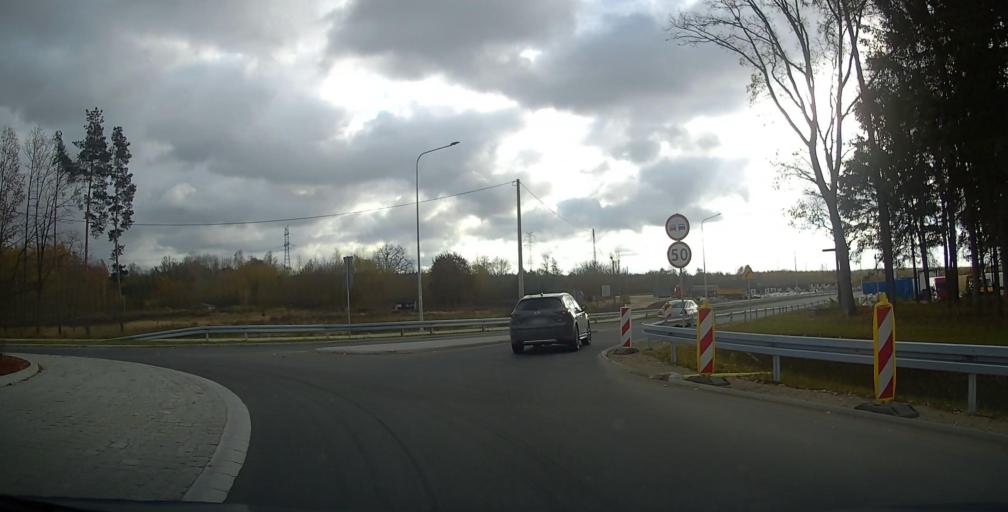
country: PL
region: Warmian-Masurian Voivodeship
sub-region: Powiat elcki
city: Elk
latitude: 53.8376
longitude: 22.4155
